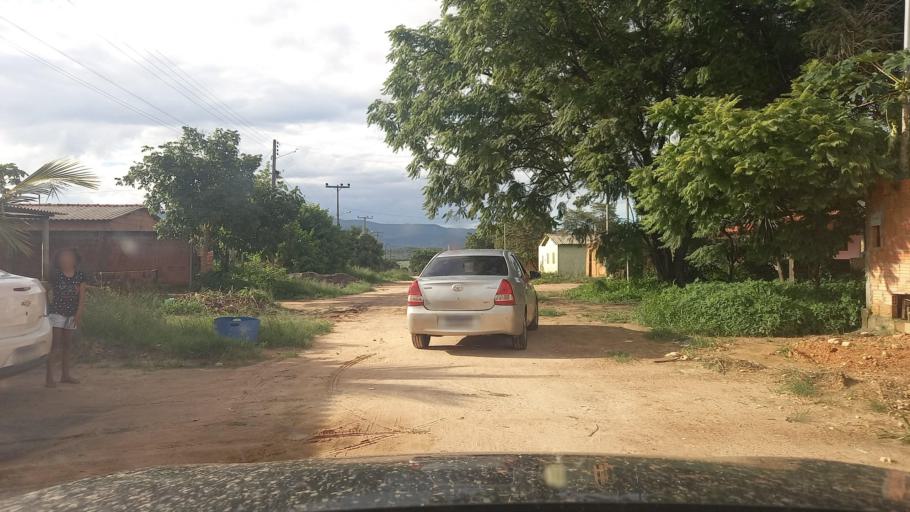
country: BR
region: Goias
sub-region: Cavalcante
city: Cavalcante
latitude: -13.8002
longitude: -47.4420
